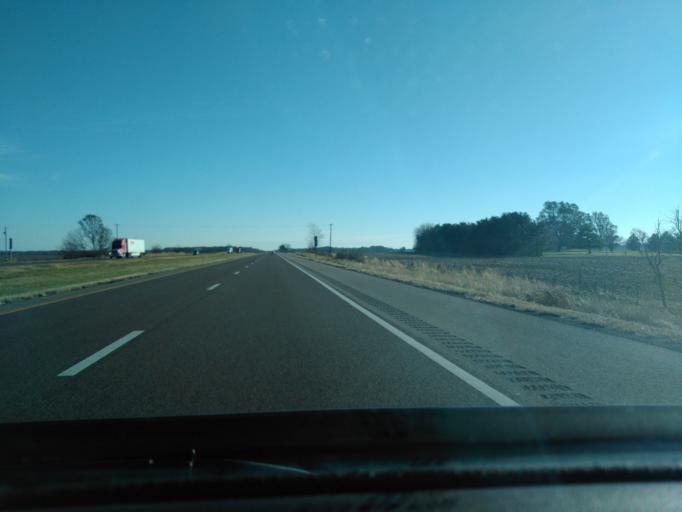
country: US
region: Illinois
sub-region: Madison County
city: Highland
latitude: 38.7846
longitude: -89.7242
